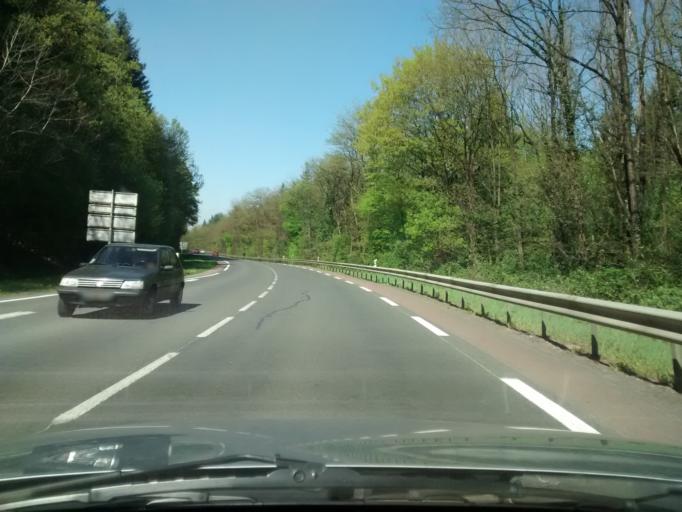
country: FR
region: Pays de la Loire
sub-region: Departement de la Sarthe
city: Brulon
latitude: 48.0262
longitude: -0.2382
